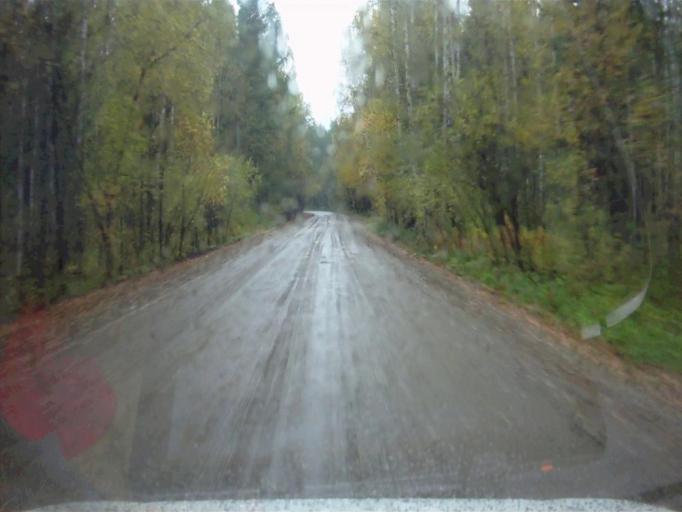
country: RU
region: Chelyabinsk
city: Kyshtym
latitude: 55.8906
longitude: 60.4652
